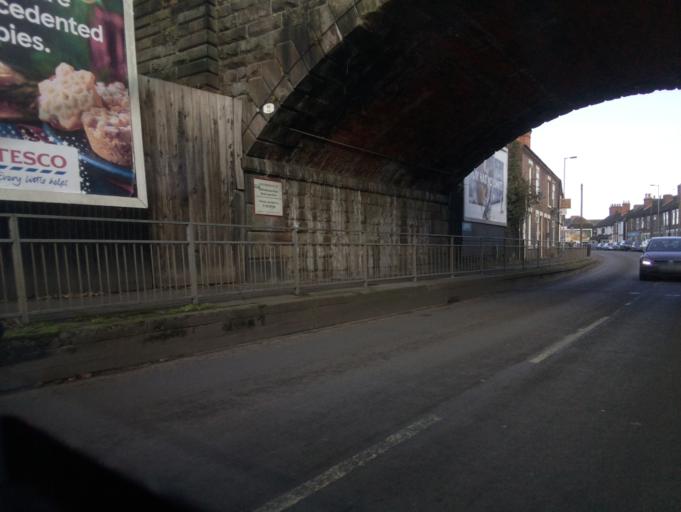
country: GB
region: England
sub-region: Staffordshire
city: Burton upon Trent
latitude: 52.7907
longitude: -1.6447
